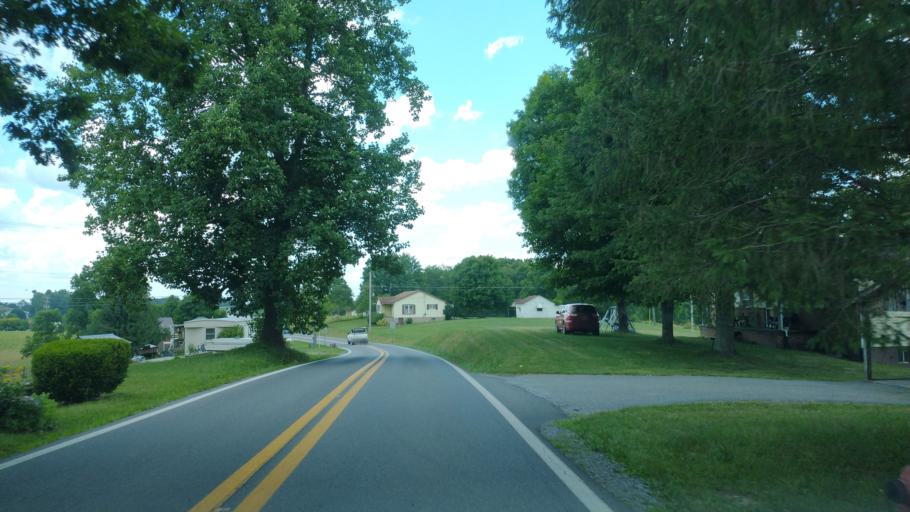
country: US
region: West Virginia
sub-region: Mercer County
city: Athens
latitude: 37.4040
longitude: -81.0593
